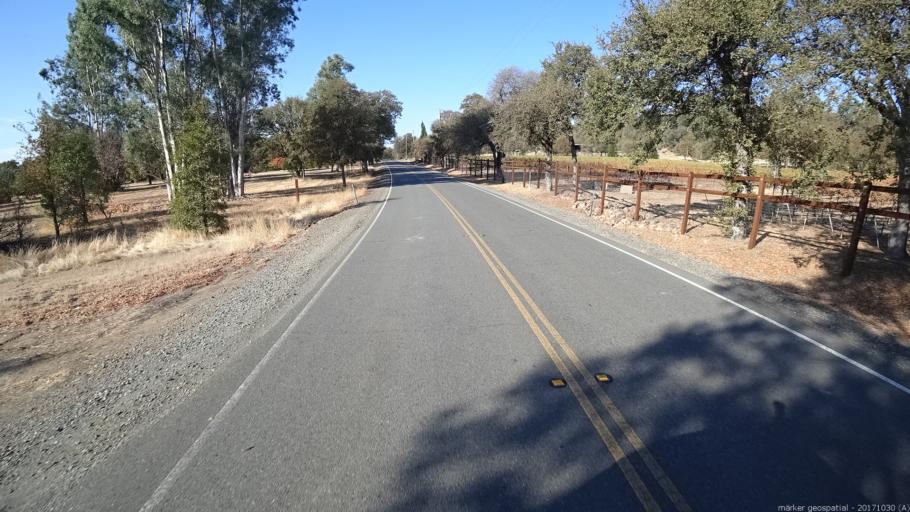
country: US
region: California
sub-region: Shasta County
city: Palo Cedro
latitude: 40.5678
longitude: -122.1974
